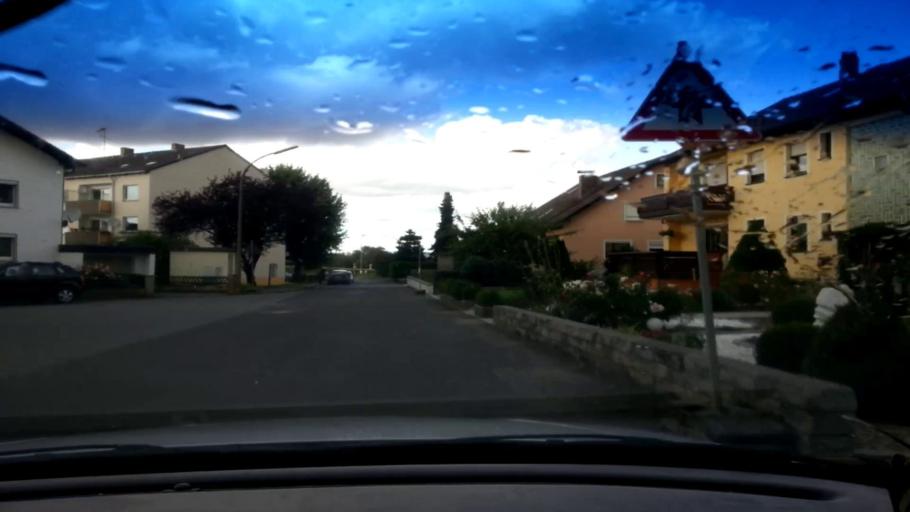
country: DE
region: Bavaria
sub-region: Upper Franconia
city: Zapfendorf
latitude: 50.0220
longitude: 10.9382
